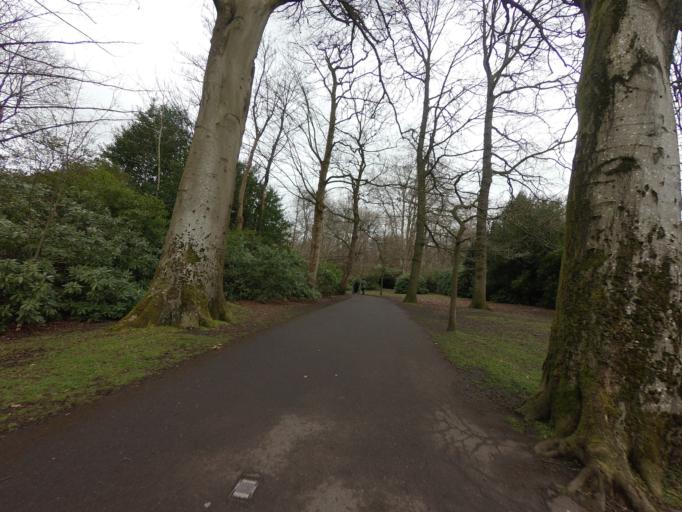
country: GB
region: Scotland
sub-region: East Renfrewshire
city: Giffnock
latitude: 55.8310
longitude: -4.2756
